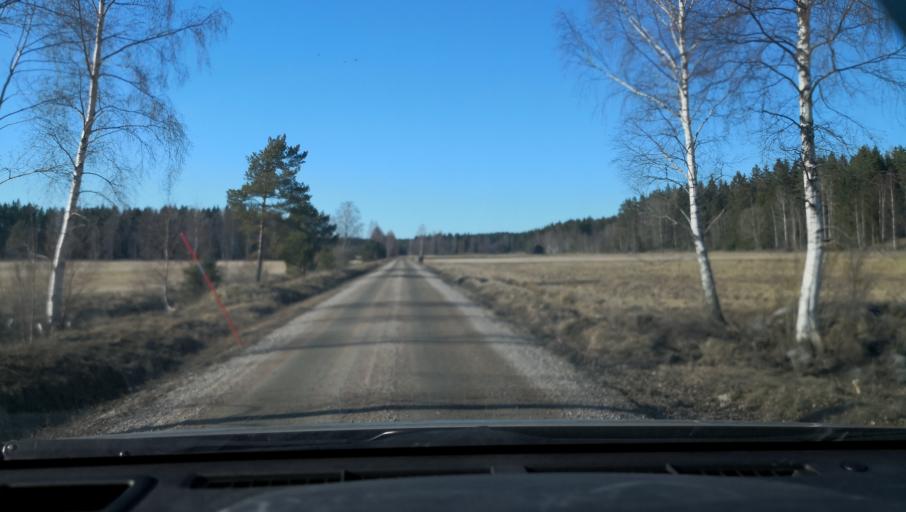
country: SE
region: Vaestmanland
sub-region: Sala Kommun
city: Sala
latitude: 60.1260
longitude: 16.6555
